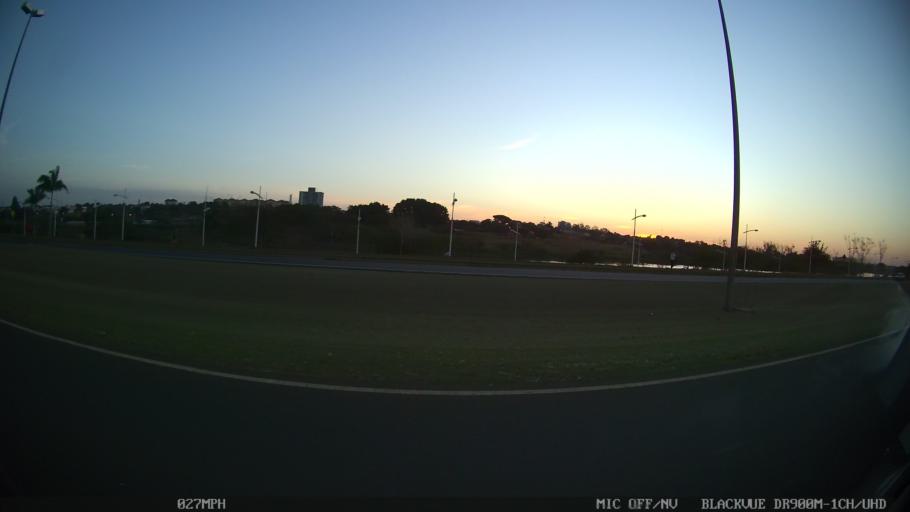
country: BR
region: Sao Paulo
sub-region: Sao Jose Do Rio Preto
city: Sao Jose do Rio Preto
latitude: -20.8229
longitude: -49.3442
